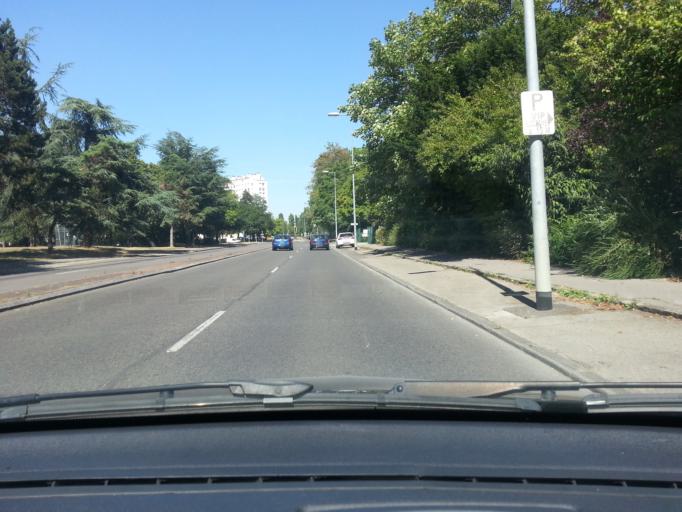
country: FR
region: Bourgogne
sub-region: Departement de la Cote-d'Or
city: Saint-Apollinaire
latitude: 47.3262
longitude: 5.0664
